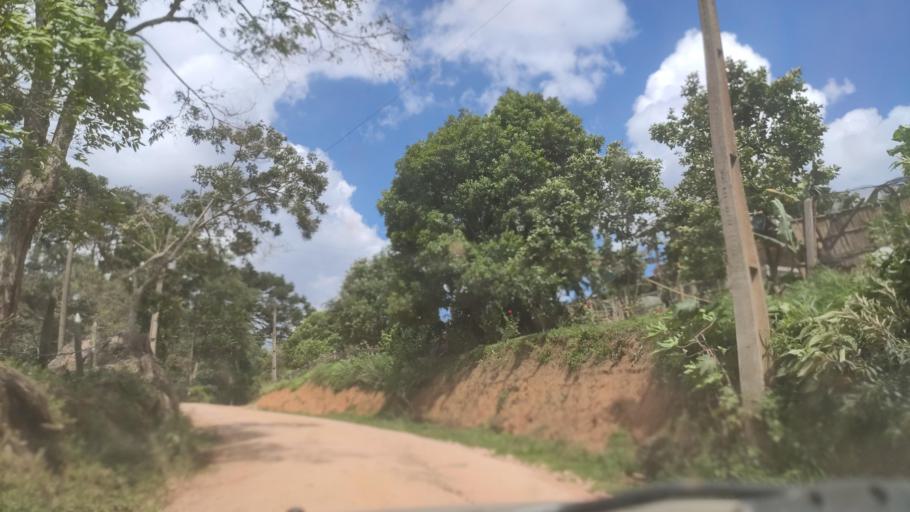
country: BR
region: Minas Gerais
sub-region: Camanducaia
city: Camanducaia
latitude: -22.7711
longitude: -46.0062
